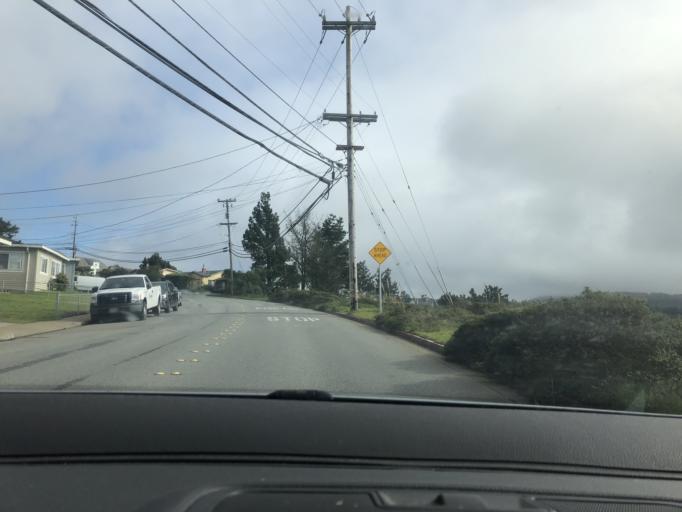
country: US
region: California
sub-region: San Mateo County
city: Pacifica
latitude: 37.6457
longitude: -122.4754
